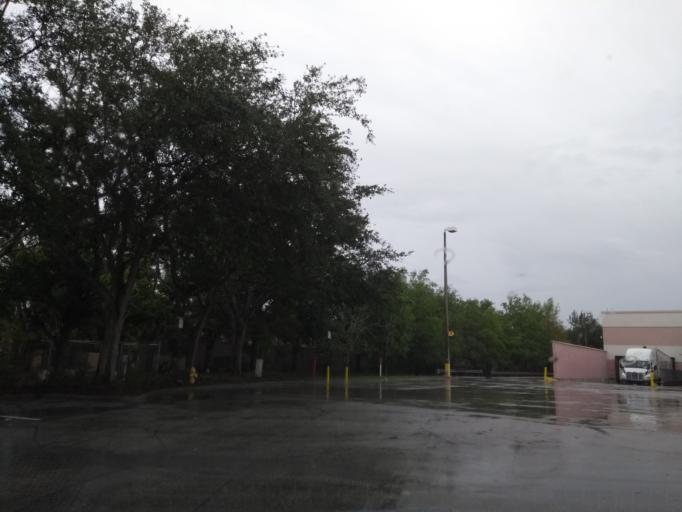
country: US
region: Florida
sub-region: Collier County
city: Pine Ridge
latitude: 26.2081
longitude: -81.7662
